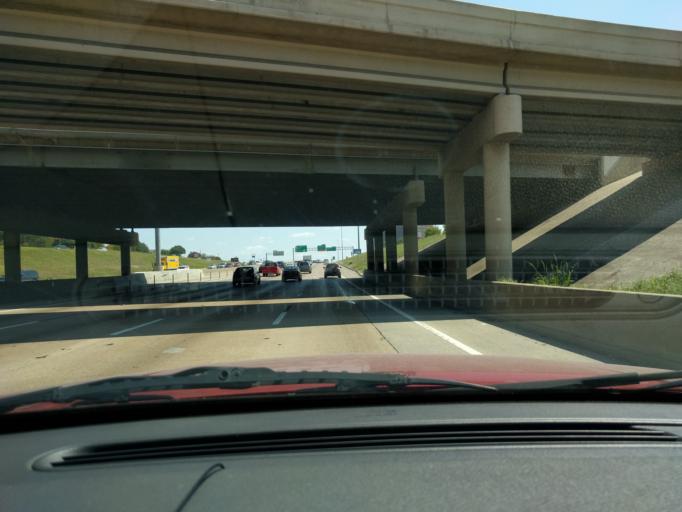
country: US
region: Texas
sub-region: Dallas County
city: Richardson
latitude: 32.9168
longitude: -96.7437
